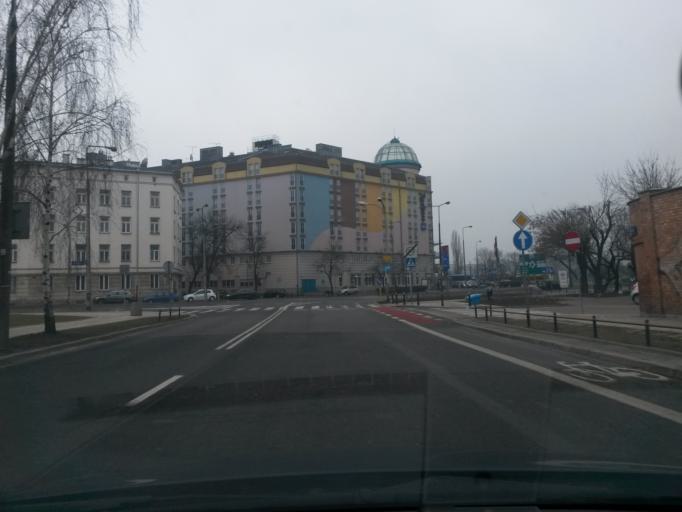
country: PL
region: Masovian Voivodeship
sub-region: Warszawa
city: Ochota
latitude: 52.2238
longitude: 20.9908
